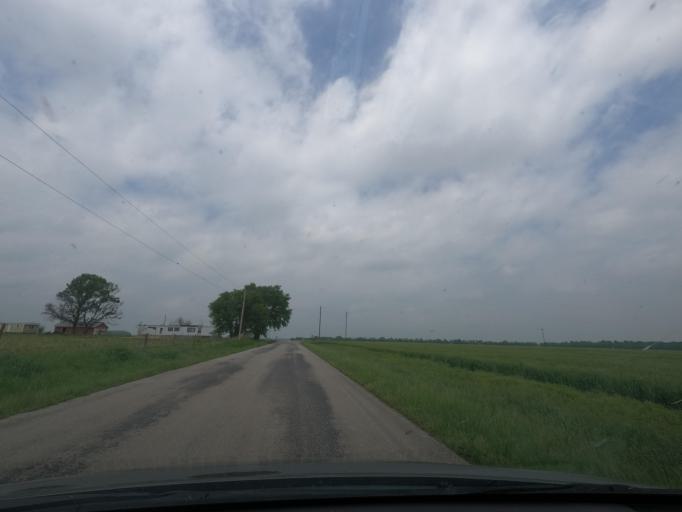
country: US
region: Kansas
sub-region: Cherokee County
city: Columbus
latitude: 37.2809
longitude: -94.9406
